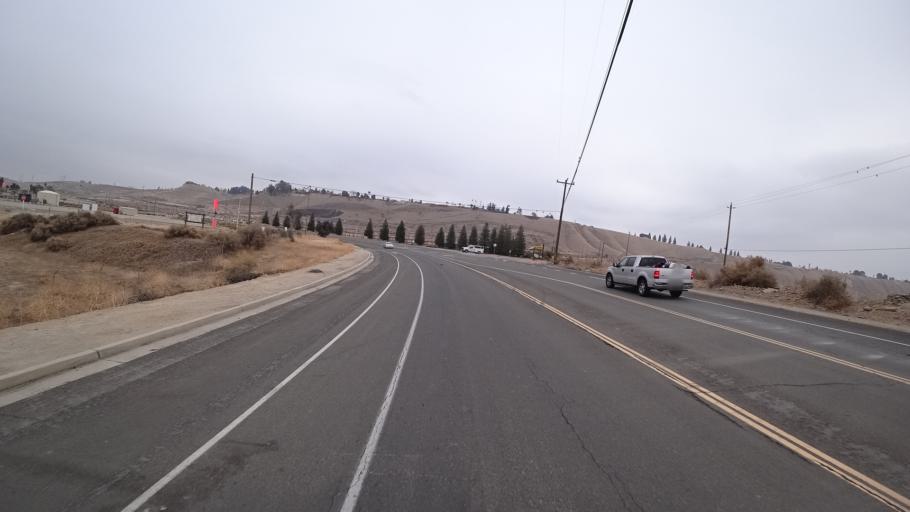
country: US
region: California
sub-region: Kern County
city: Oildale
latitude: 35.4207
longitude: -118.9674
